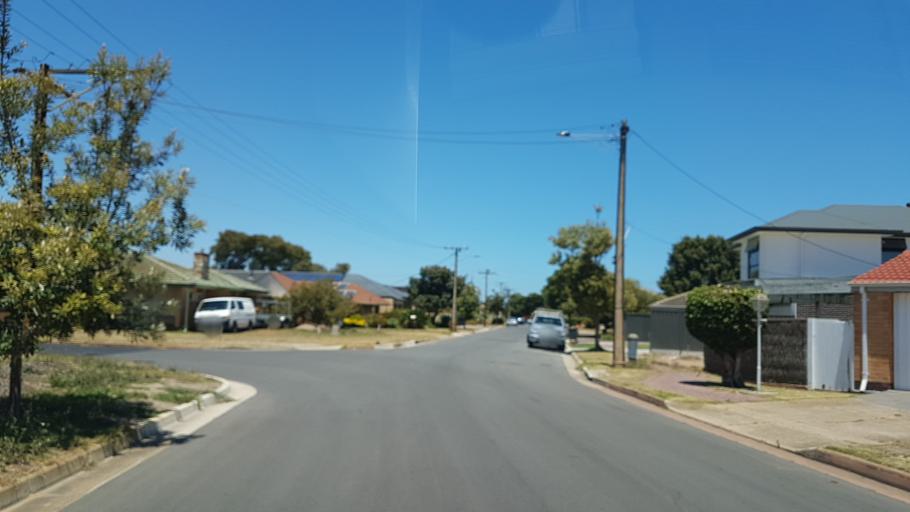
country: AU
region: South Australia
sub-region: Charles Sturt
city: West Lakes Shore
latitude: -34.8536
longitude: 138.4813
